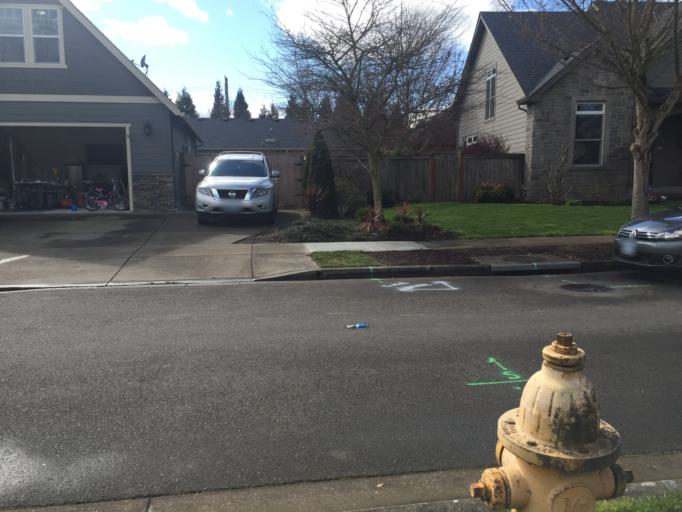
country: US
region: Oregon
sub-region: Lane County
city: Eugene
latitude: 44.1004
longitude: -123.1552
